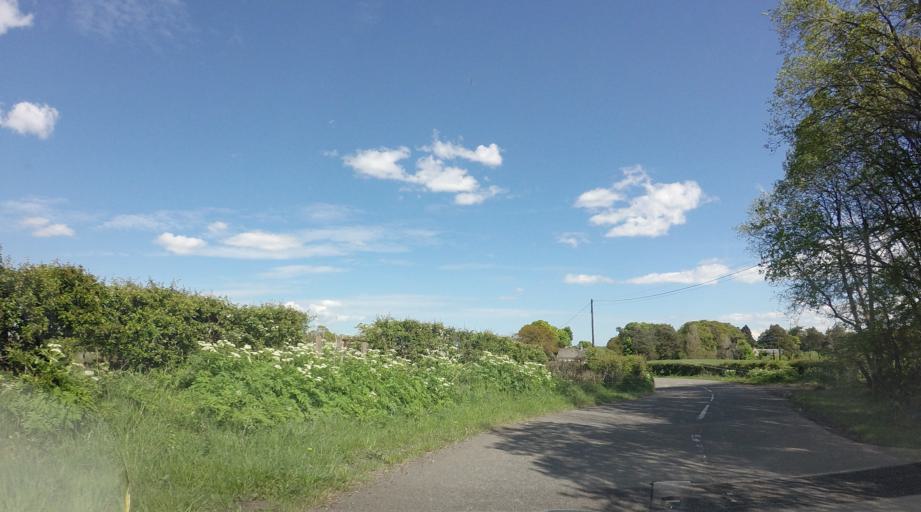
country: GB
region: Scotland
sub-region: West Lothian
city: Linlithgow
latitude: 55.9706
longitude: -3.6570
